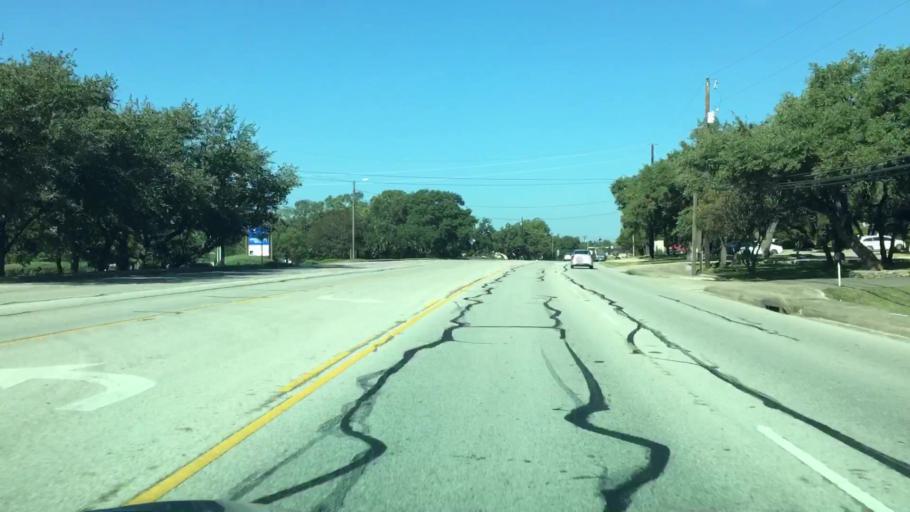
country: US
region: Texas
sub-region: Hays County
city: Dripping Springs
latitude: 30.1927
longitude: -98.0984
